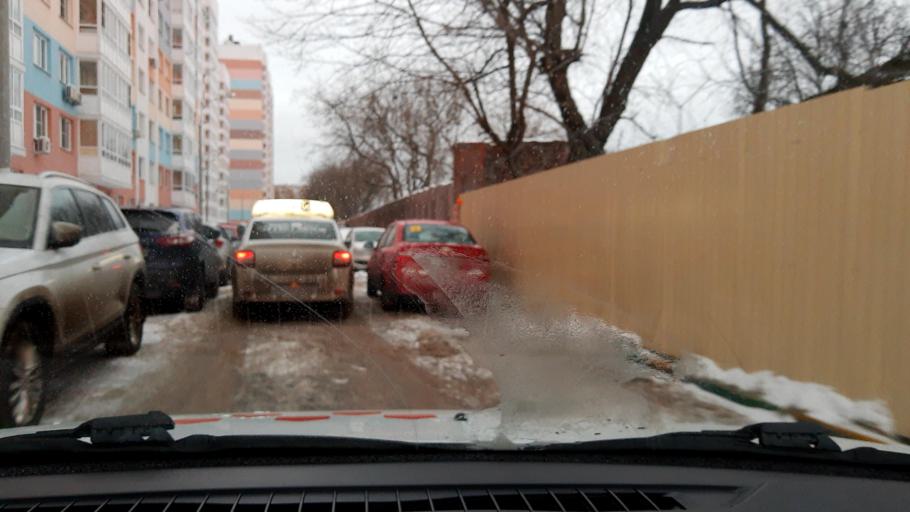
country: RU
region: Nizjnij Novgorod
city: Nizhniy Novgorod
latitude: 56.2841
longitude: 43.9882
